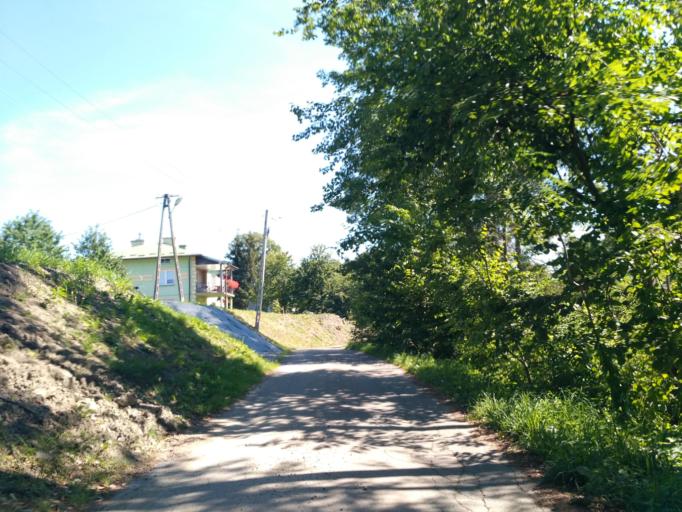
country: PL
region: Subcarpathian Voivodeship
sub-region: Powiat brzozowski
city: Gorki
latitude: 49.6196
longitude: 22.0156
